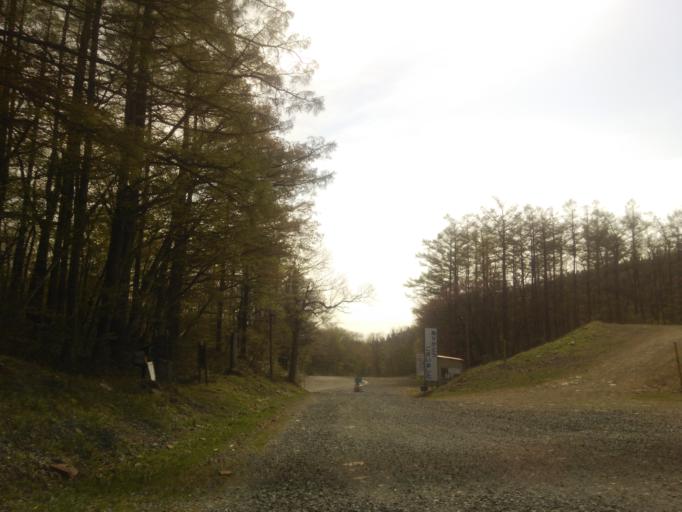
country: JP
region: Fukushima
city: Nihommatsu
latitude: 37.6408
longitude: 140.3314
